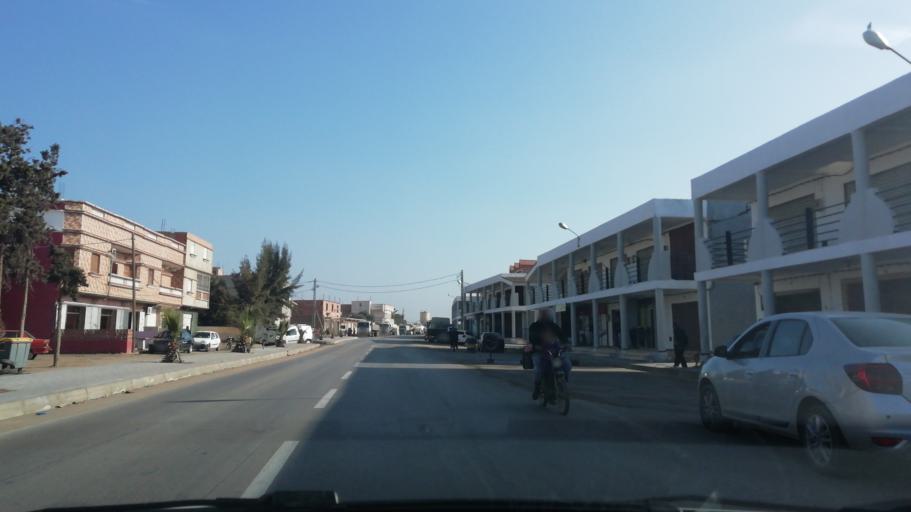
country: DZ
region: Mostaganem
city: Mostaganem
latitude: 35.7381
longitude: -0.0301
